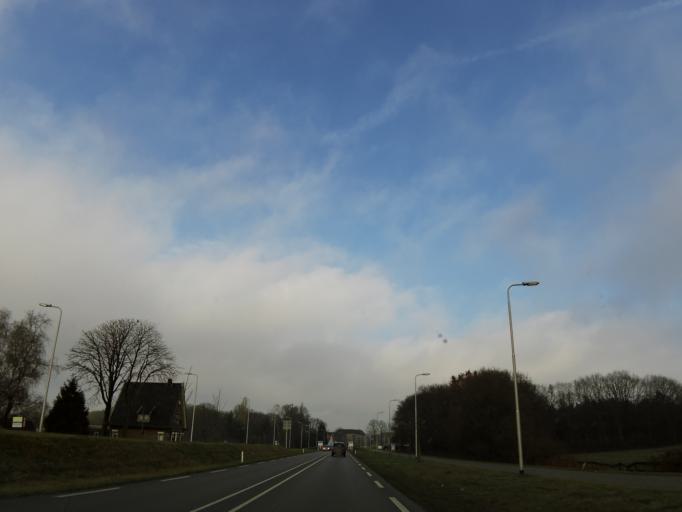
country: NL
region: Gelderland
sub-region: Gemeente Wijchen
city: Wijchen
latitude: 51.7991
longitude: 5.7536
